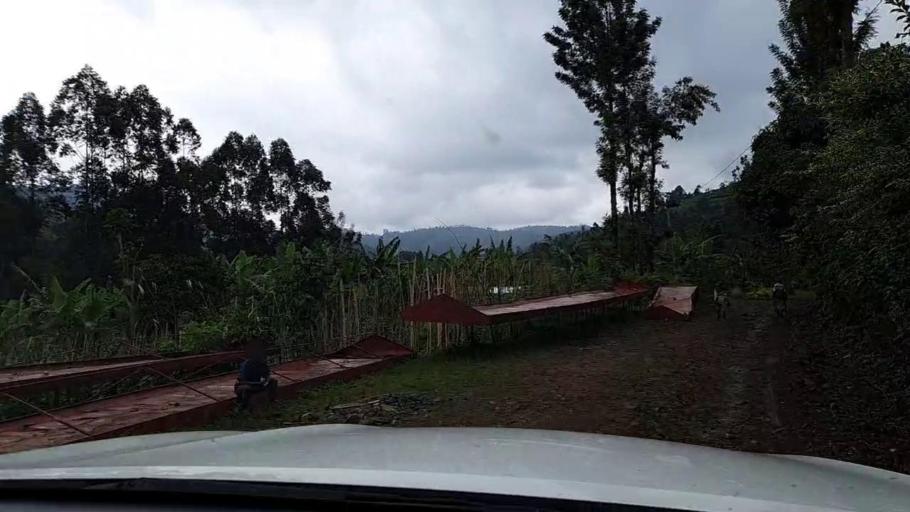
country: RW
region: Western Province
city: Cyangugu
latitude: -2.5388
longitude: 29.0393
